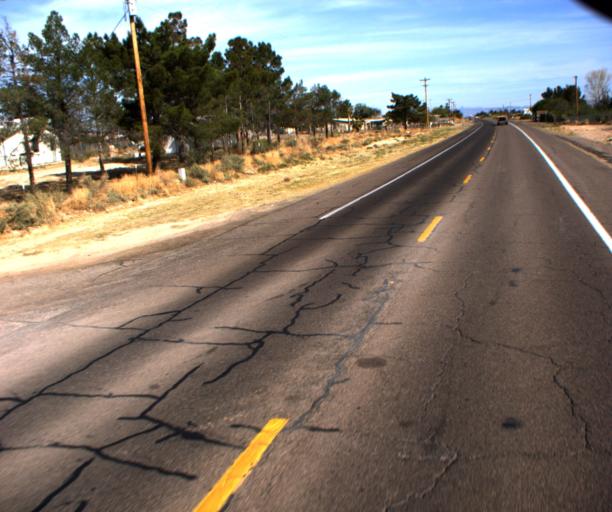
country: US
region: Arizona
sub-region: Graham County
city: Swift Trail Junction
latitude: 32.7190
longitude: -109.7094
